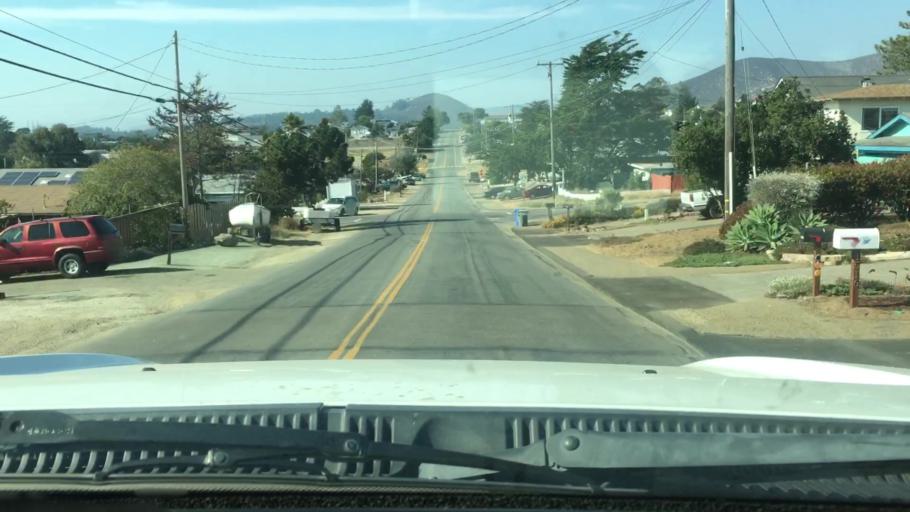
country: US
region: California
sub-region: San Luis Obispo County
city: Los Osos
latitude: 35.3238
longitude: -120.8311
